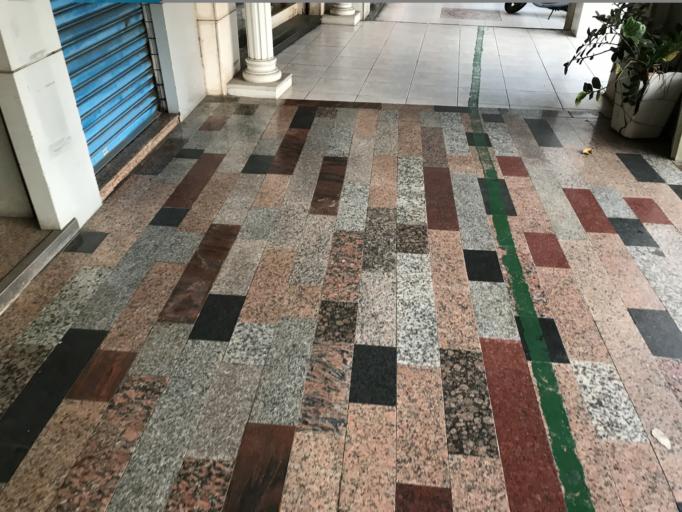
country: TW
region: Taiwan
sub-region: Tainan
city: Tainan
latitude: 22.9931
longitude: 120.2054
